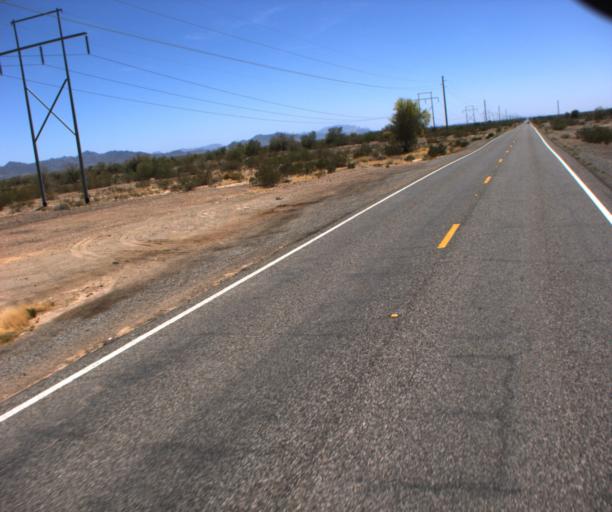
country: US
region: Arizona
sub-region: La Paz County
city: Quartzsite
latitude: 33.7320
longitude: -114.2171
